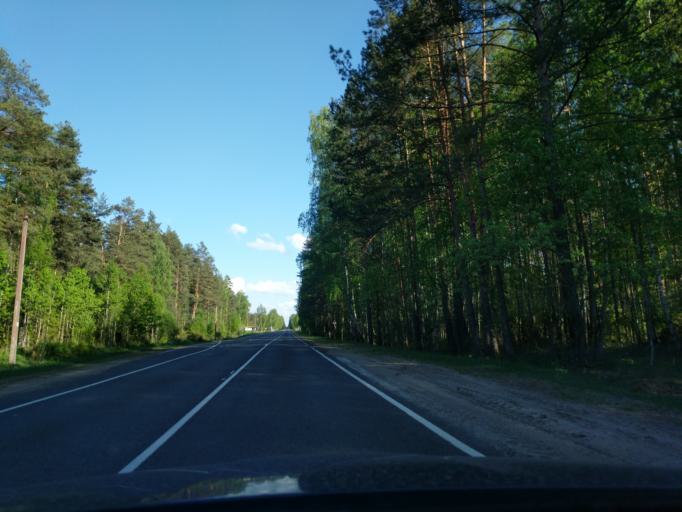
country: BY
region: Minsk
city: Myadzyel
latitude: 54.8172
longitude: 26.9658
